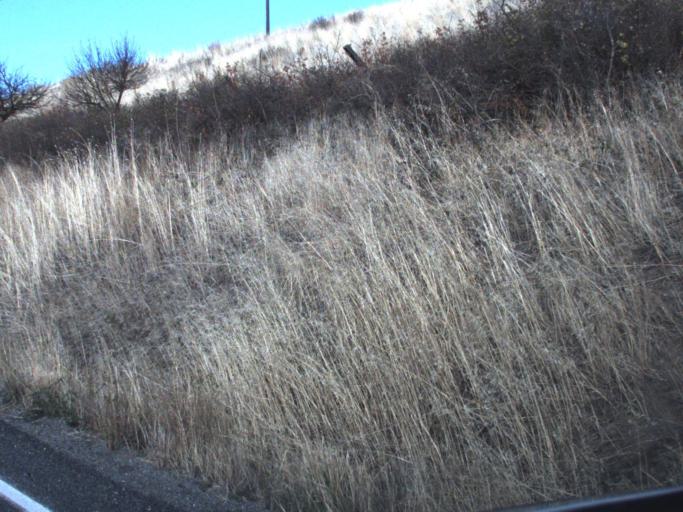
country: US
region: Washington
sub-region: Stevens County
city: Kettle Falls
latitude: 48.4037
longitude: -118.1696
